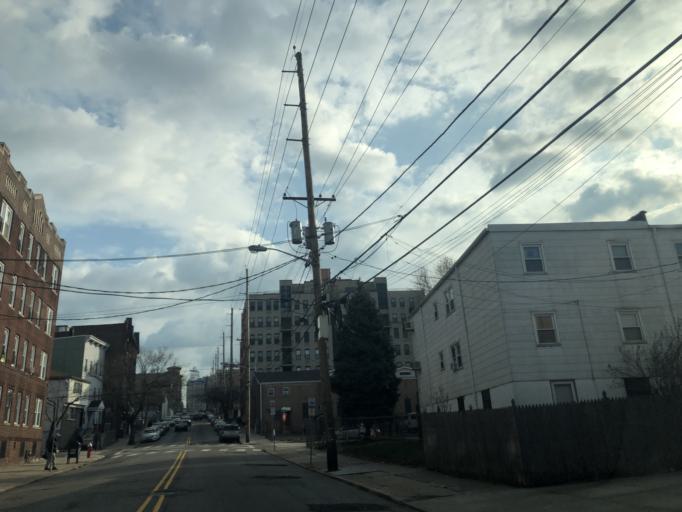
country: US
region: New Jersey
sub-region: Hudson County
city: Jersey City
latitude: 40.7323
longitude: -74.0723
